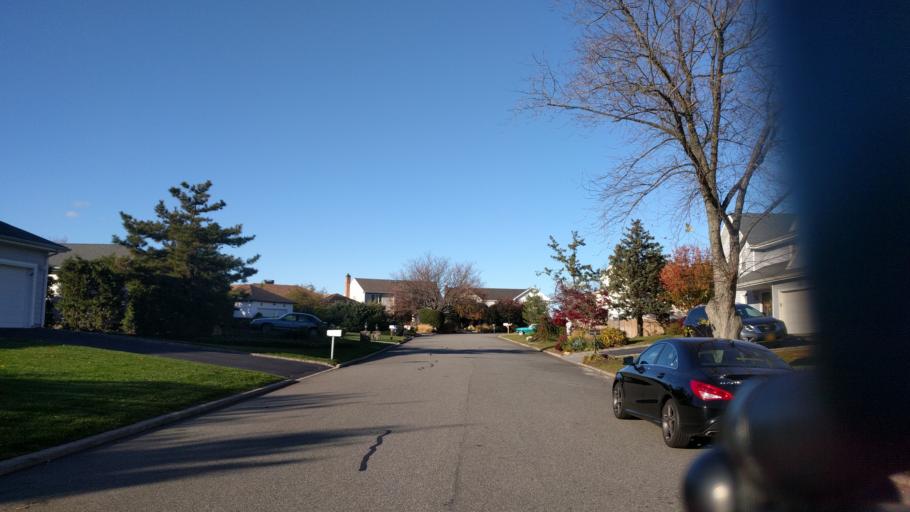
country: US
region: New York
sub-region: Nassau County
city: Bayville
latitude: 40.9139
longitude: -73.5665
